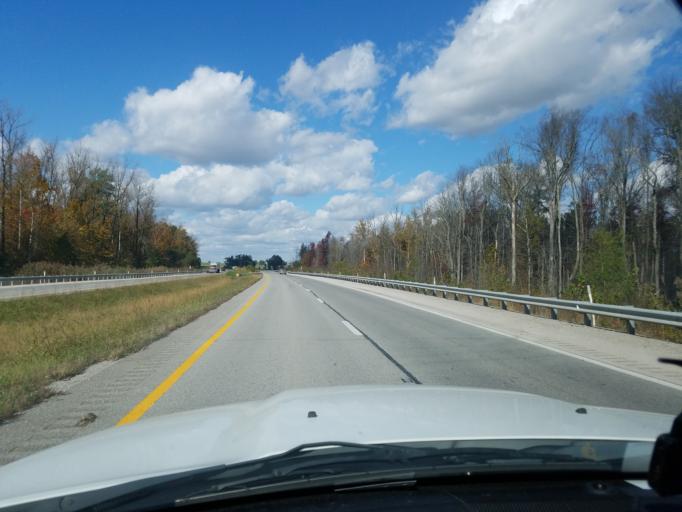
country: US
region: Kentucky
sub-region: Daviess County
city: Masonville
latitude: 37.6515
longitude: -87.0018
